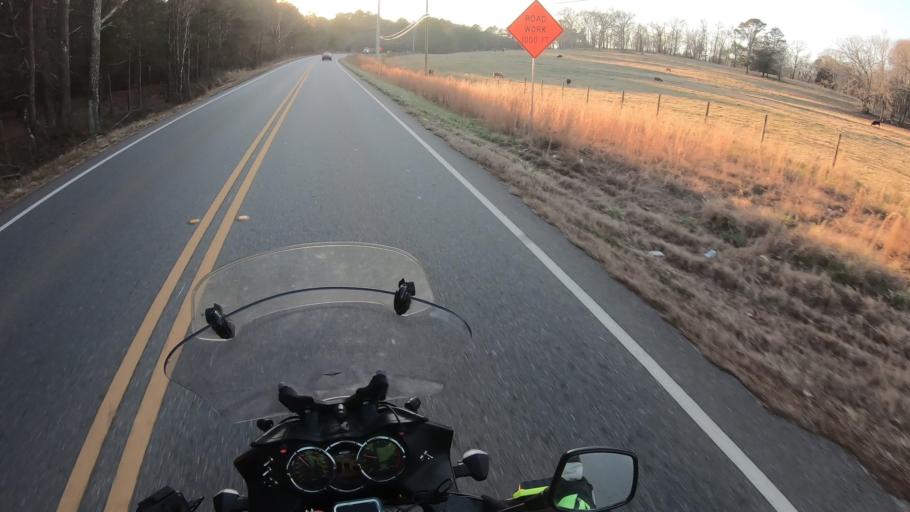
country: US
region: Georgia
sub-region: Dawson County
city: Dawsonville
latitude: 34.3508
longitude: -84.1073
